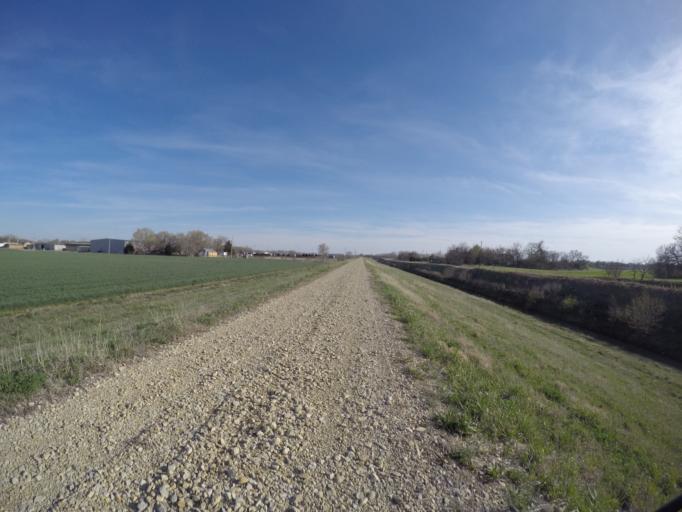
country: US
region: Kansas
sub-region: Saline County
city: Salina
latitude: 38.8536
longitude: -97.6304
